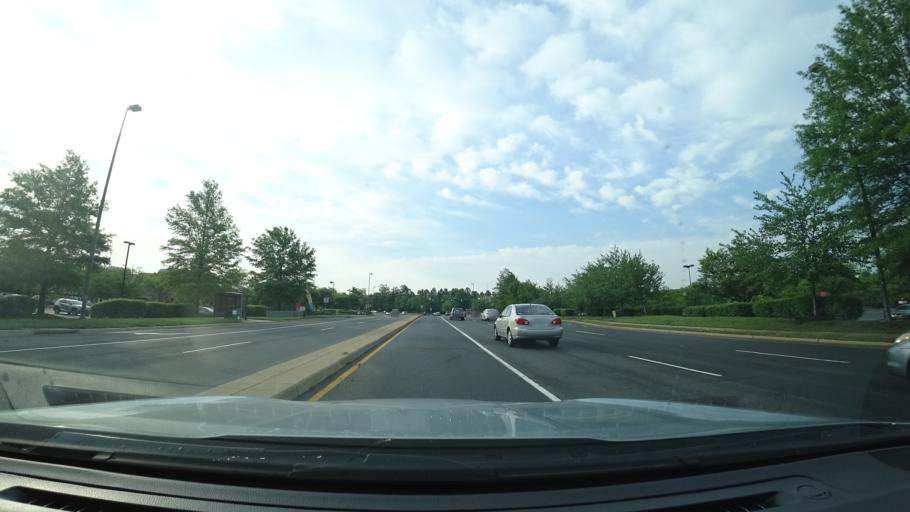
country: US
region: Virginia
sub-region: Fairfax County
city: Herndon
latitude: 38.9556
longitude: -77.3691
